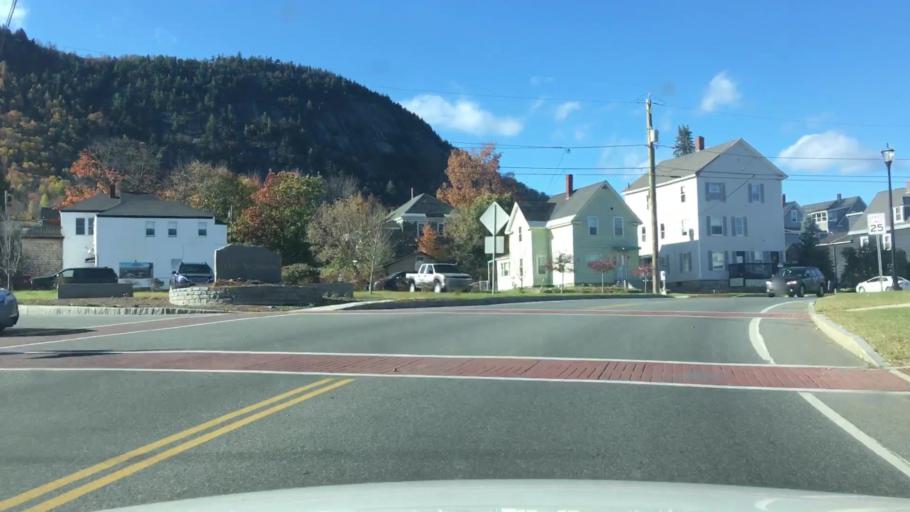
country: US
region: New Hampshire
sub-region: Coos County
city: Berlin
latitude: 44.4699
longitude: -71.1859
